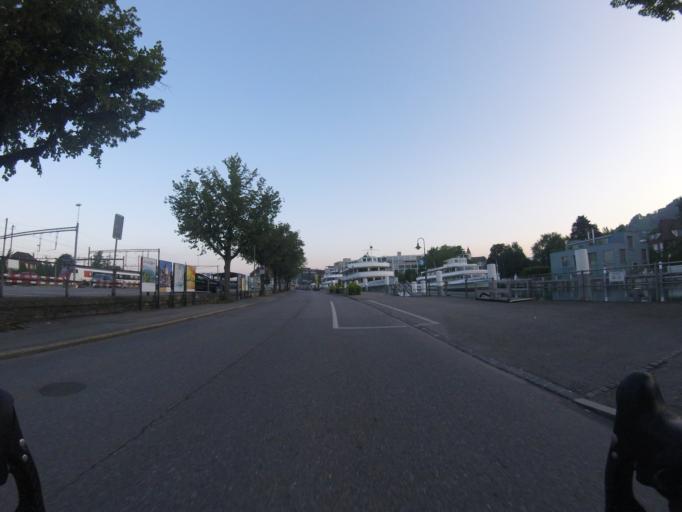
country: CH
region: Bern
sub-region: Thun District
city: Thun
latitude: 46.7531
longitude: 7.6324
